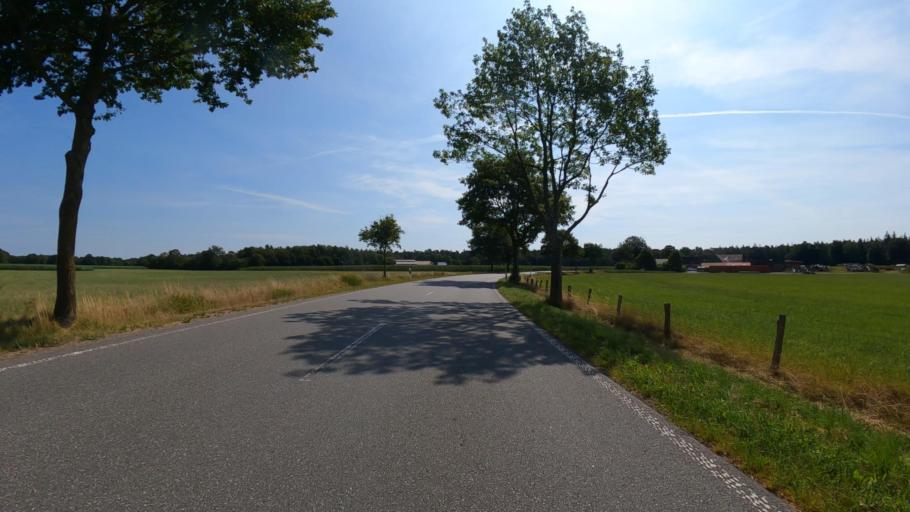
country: DE
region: Schleswig-Holstein
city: Heidmuhlen
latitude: 53.9665
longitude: 10.1169
